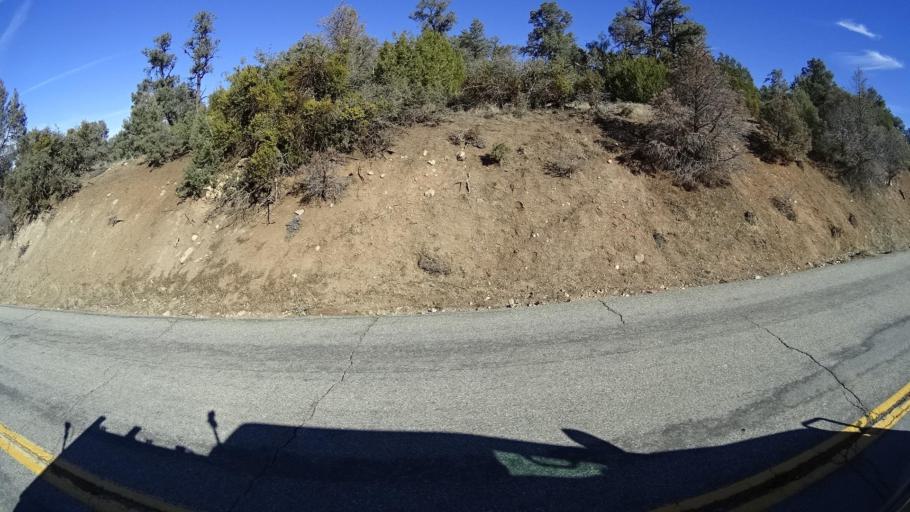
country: US
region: California
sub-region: Kern County
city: Pine Mountain Club
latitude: 34.8705
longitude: -119.3038
